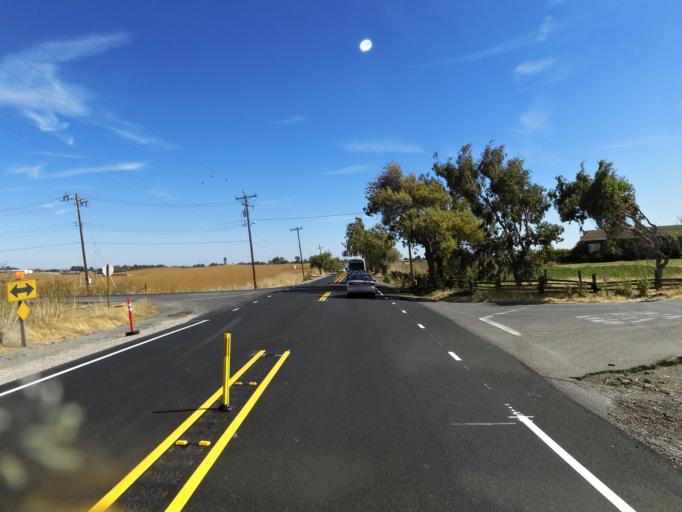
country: US
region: California
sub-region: Solano County
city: Rio Vista
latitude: 38.1708
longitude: -121.7096
